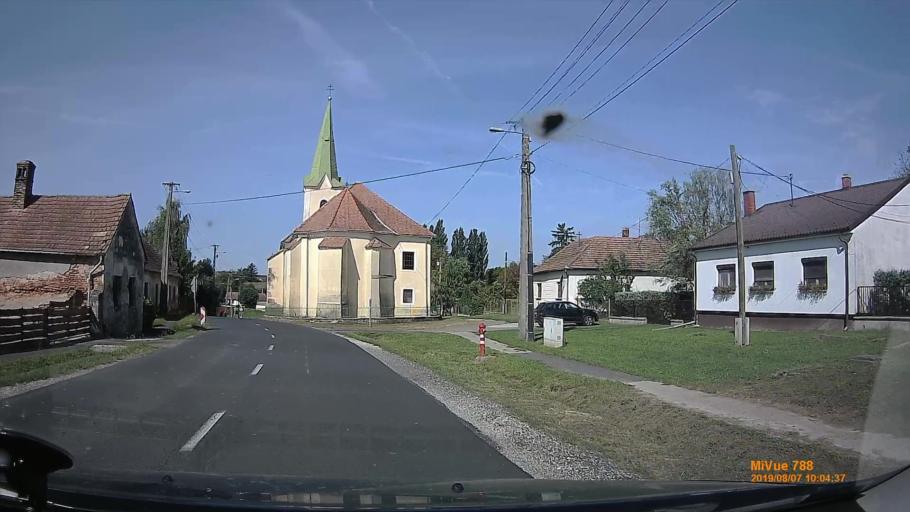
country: HU
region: Zala
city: Zalaegerszeg
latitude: 46.7010
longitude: 16.7582
